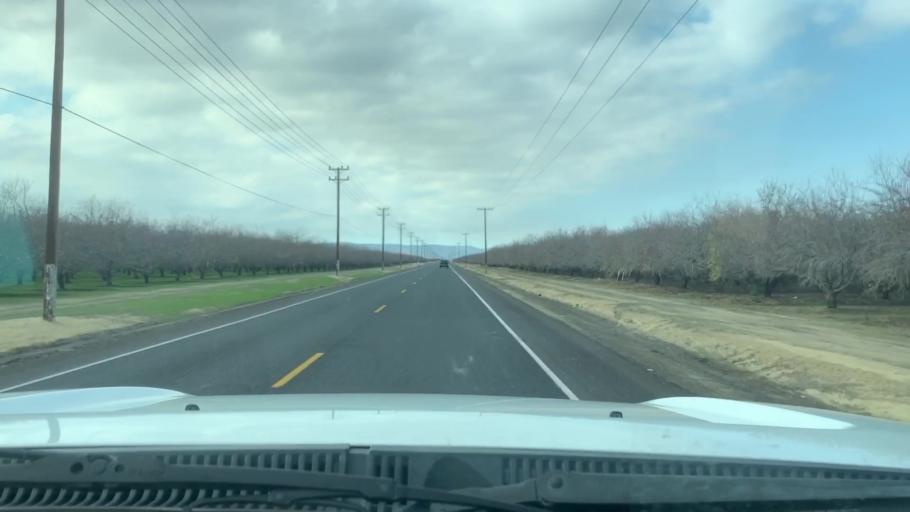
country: US
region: California
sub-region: Kern County
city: Lost Hills
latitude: 35.4993
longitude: -119.6770
